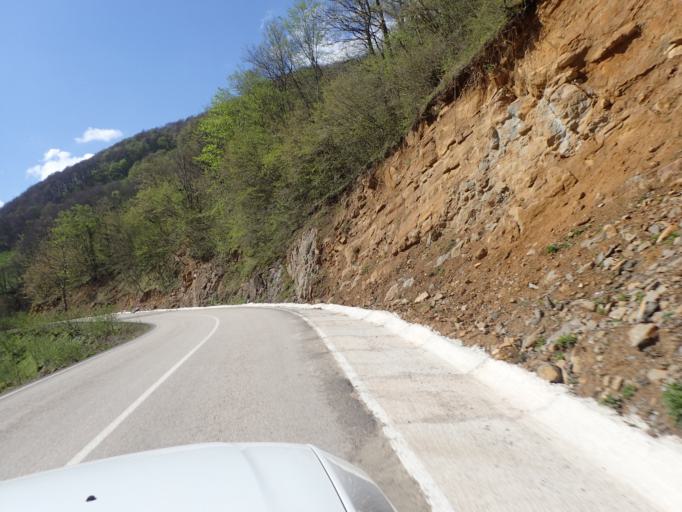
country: TR
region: Ordu
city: Korgan
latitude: 40.7729
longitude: 37.3293
